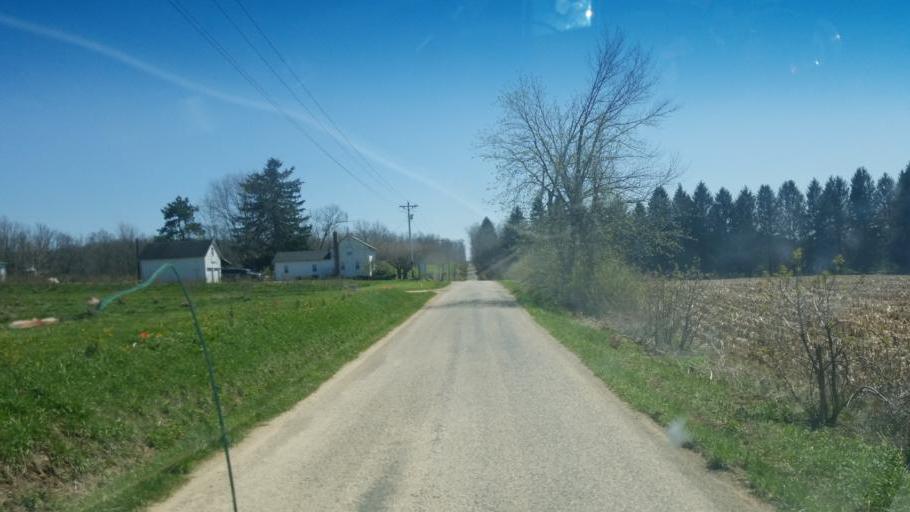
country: US
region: Ohio
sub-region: Ashland County
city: Ashland
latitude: 40.8325
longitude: -82.3877
